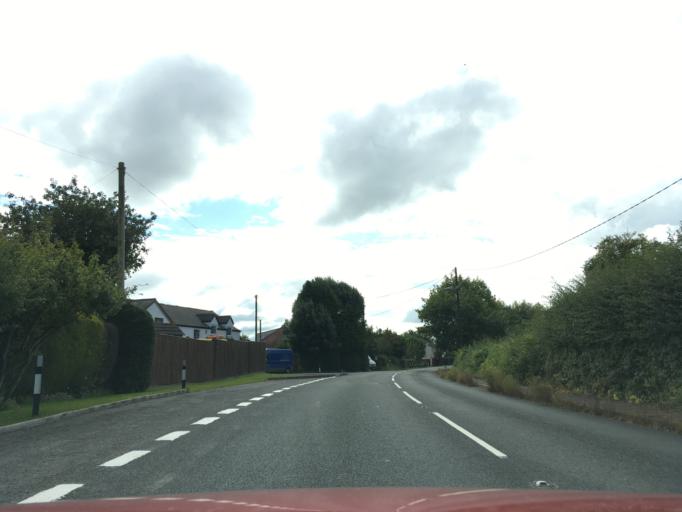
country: GB
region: Wales
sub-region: Monmouthshire
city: Chepstow
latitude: 51.6265
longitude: -2.6532
